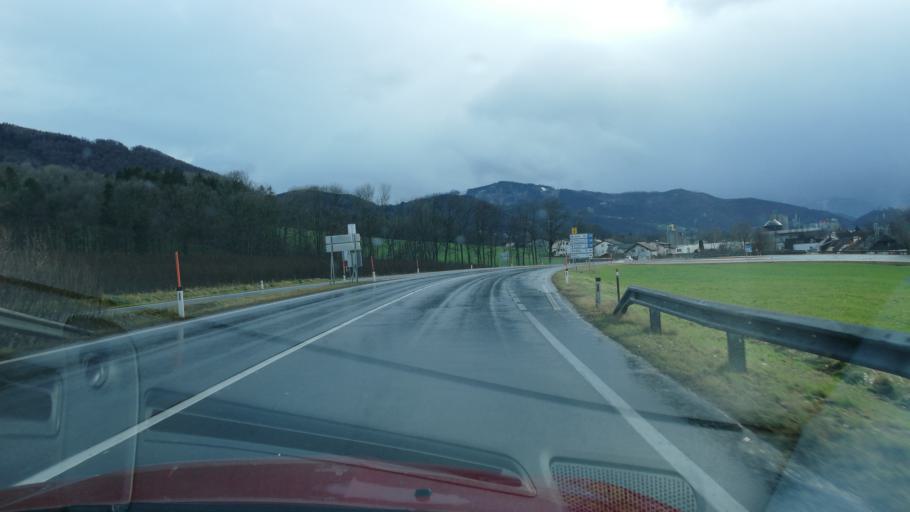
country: AT
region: Upper Austria
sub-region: Politischer Bezirk Kirchdorf an der Krems
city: Micheldorf in Oberoesterreich
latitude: 47.9201
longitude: 14.1066
